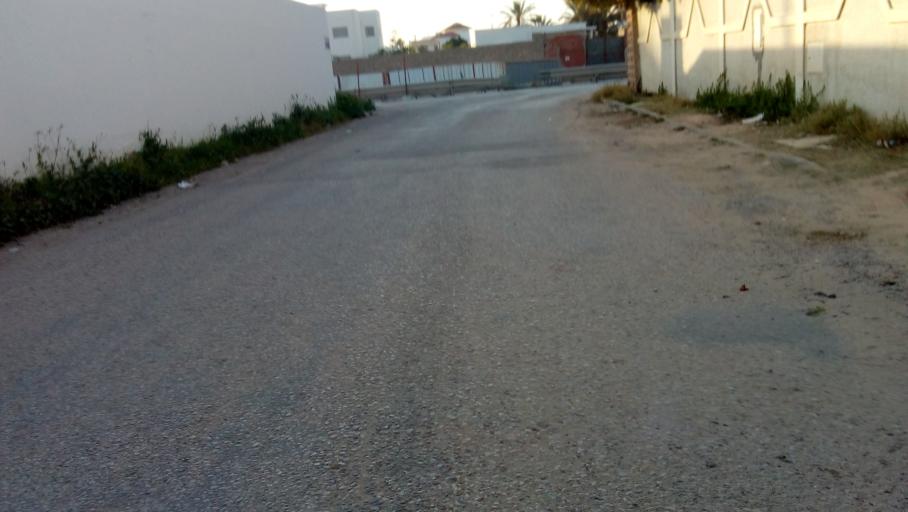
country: TN
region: Safaqis
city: Sfax
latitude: 34.7533
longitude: 10.7323
